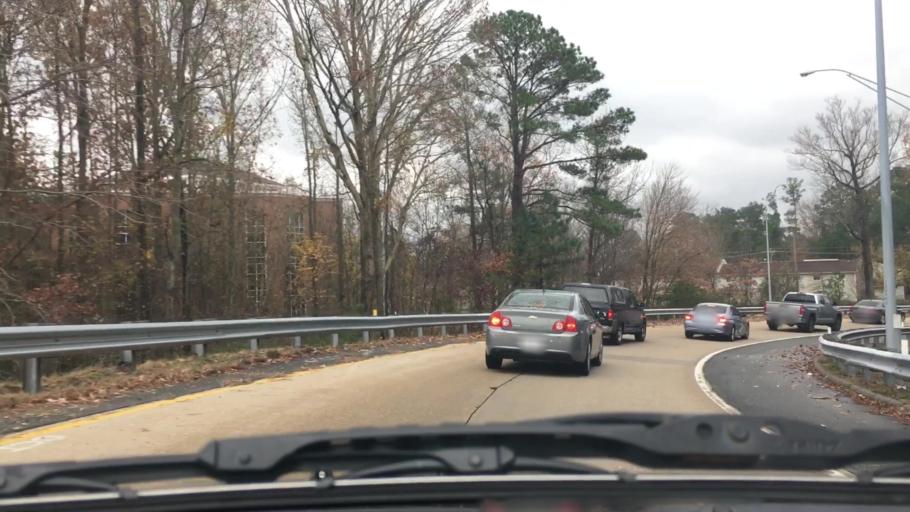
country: US
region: Virginia
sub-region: City of Chesapeake
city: Chesapeake
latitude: 36.8333
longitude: -76.1359
